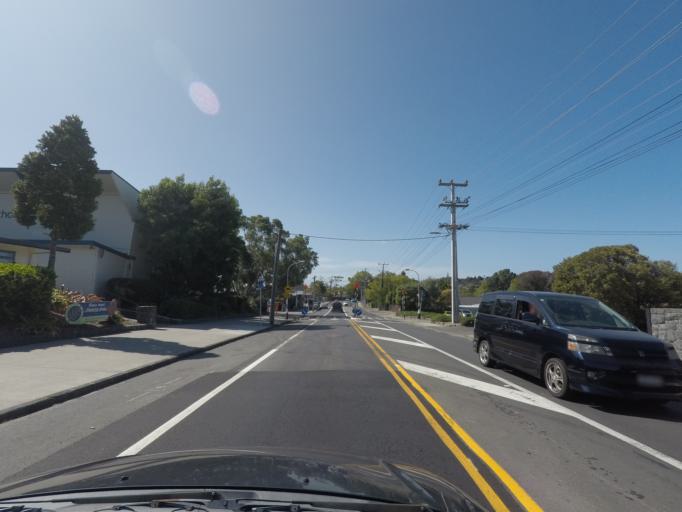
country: NZ
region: Auckland
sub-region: Auckland
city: Titirangi
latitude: -36.9280
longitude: 174.6547
